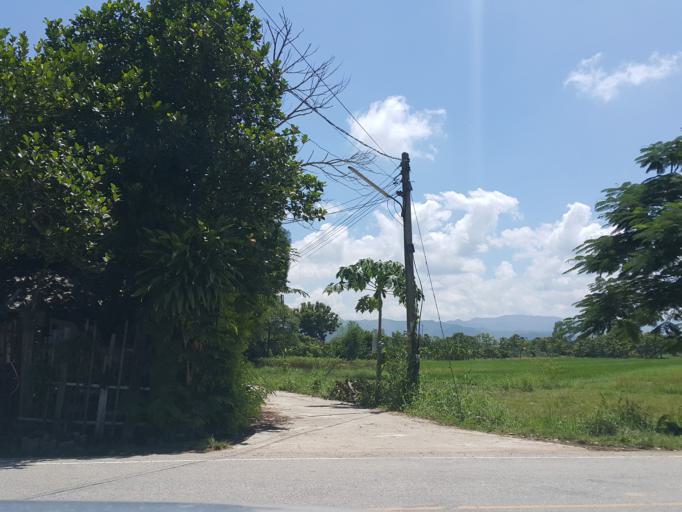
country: TH
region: Lamphun
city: Ban Thi
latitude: 18.6828
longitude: 99.1378
